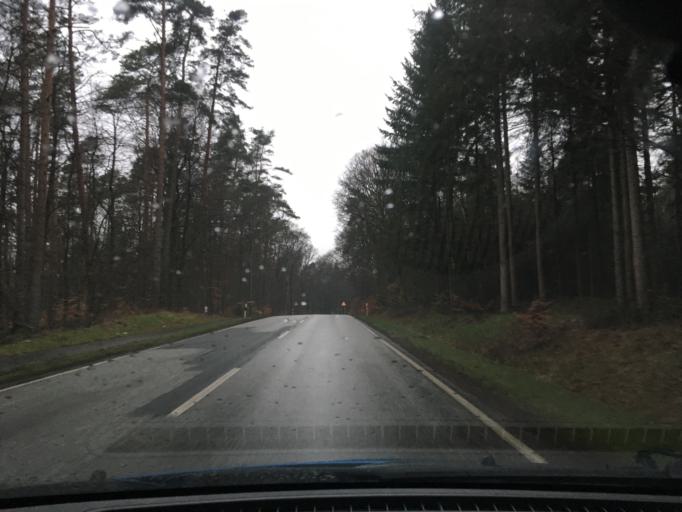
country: DE
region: Schleswig-Holstein
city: Krukow
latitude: 53.4009
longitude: 10.4556
